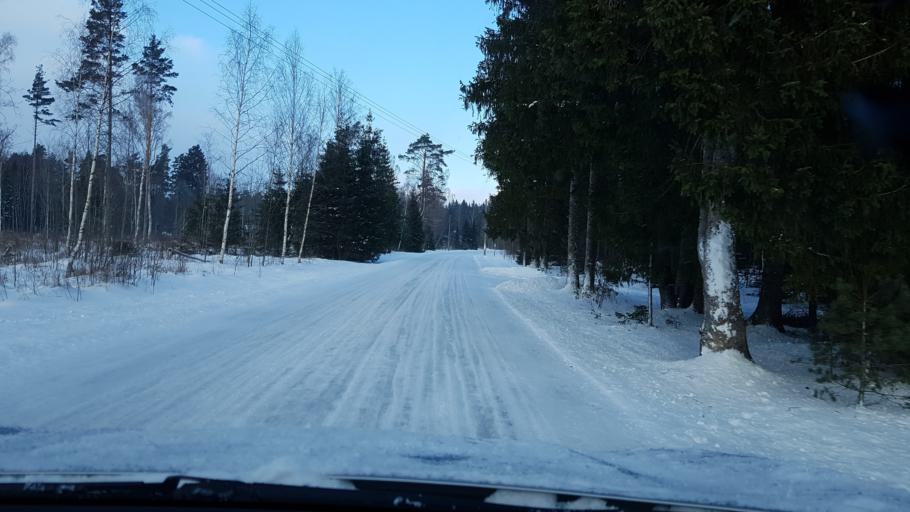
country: EE
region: Harju
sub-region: Nissi vald
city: Turba
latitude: 59.2126
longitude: 24.1412
